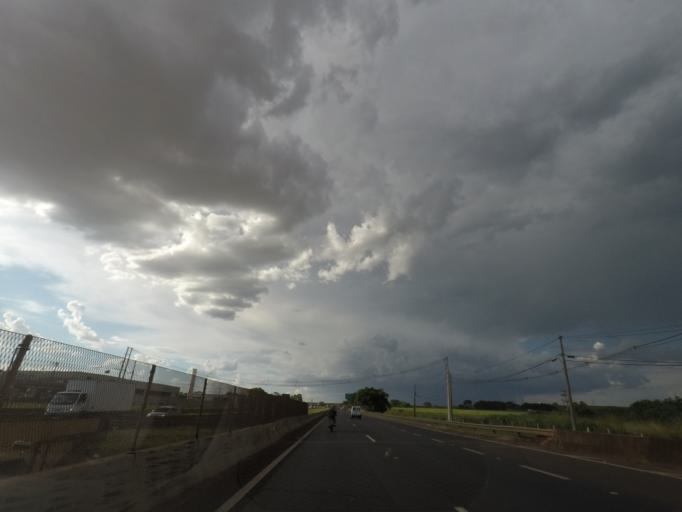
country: BR
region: Sao Paulo
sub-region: Ribeirao Preto
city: Ribeirao Preto
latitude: -21.1191
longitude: -47.7755
